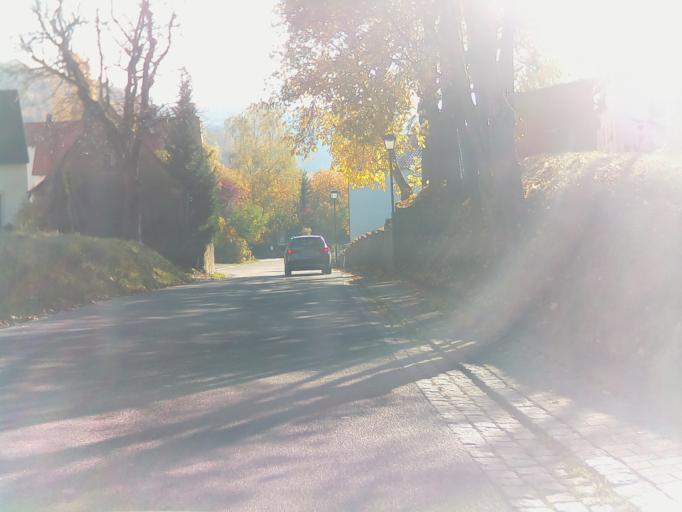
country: DE
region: Bavaria
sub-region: Regierungsbezirk Unterfranken
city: Knetzgau
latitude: 49.9079
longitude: 10.5579
